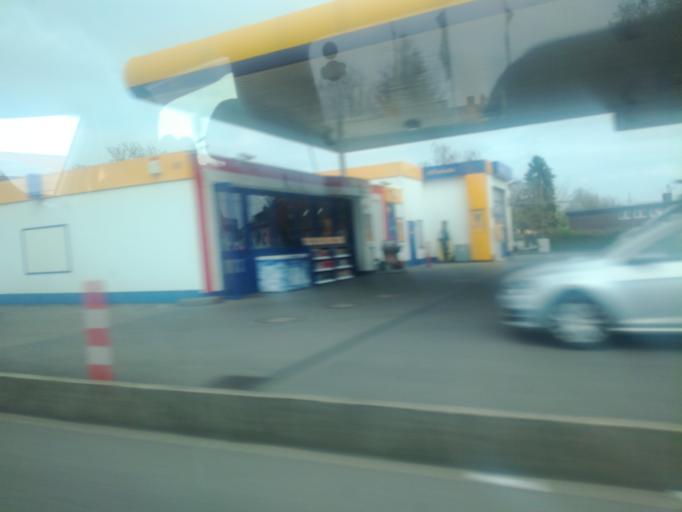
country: DE
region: North Rhine-Westphalia
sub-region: Regierungsbezirk Dusseldorf
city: Kamp-Lintfort
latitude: 51.5081
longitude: 6.5442
